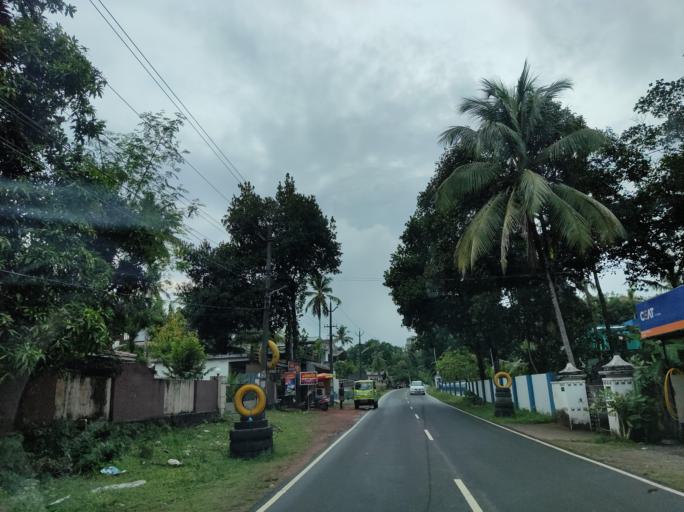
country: IN
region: Kerala
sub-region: Alappuzha
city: Mavelikara
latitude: 9.2301
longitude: 76.5708
